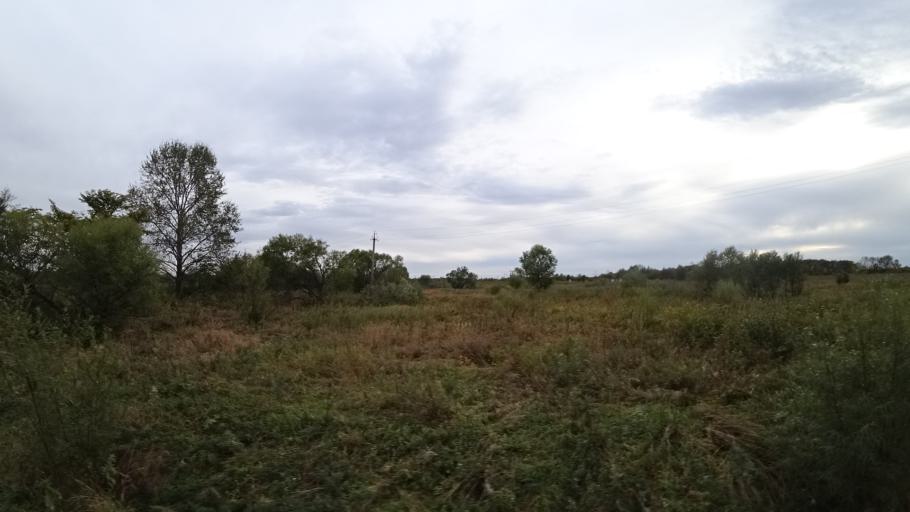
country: RU
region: Amur
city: Arkhara
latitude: 49.4364
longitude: 130.2619
